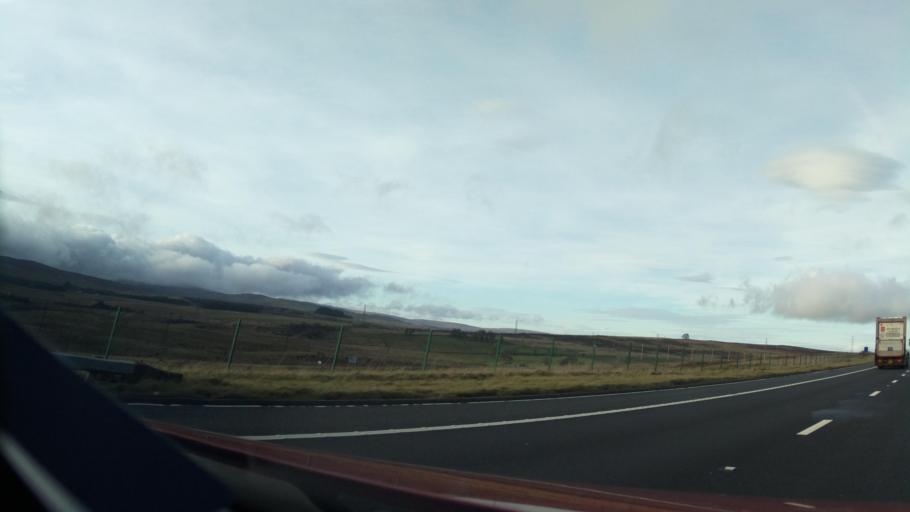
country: GB
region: England
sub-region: Cumbria
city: Appleby-in-Westmorland
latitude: 54.4851
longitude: -2.6375
